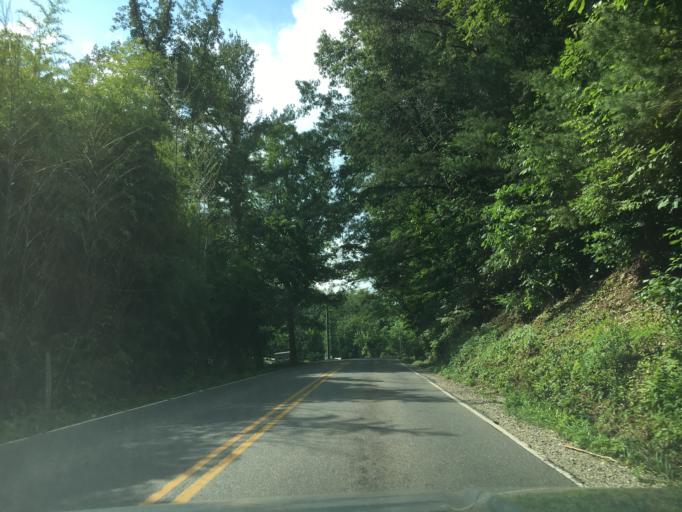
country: US
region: Virginia
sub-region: Roanoke County
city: Cave Spring
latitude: 37.2047
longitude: -80.0078
